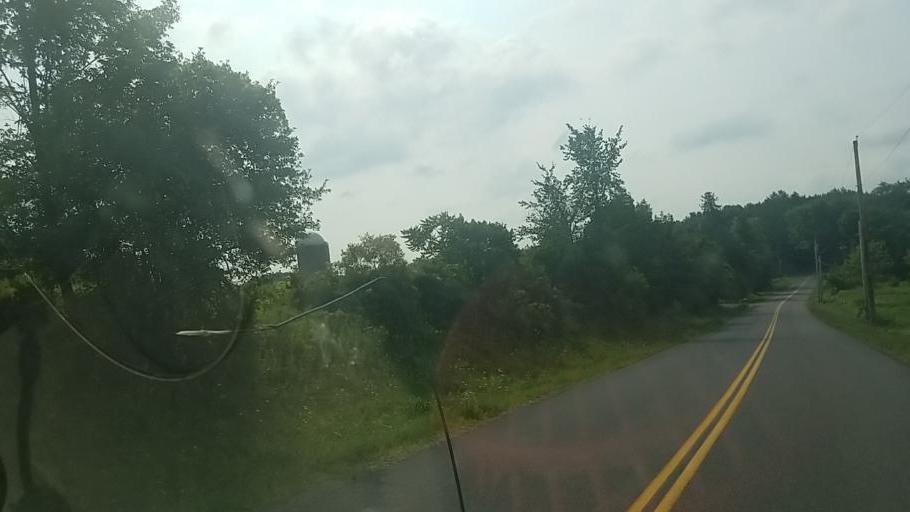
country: US
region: New York
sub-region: Fulton County
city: Johnstown
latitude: 43.0255
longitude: -74.3821
